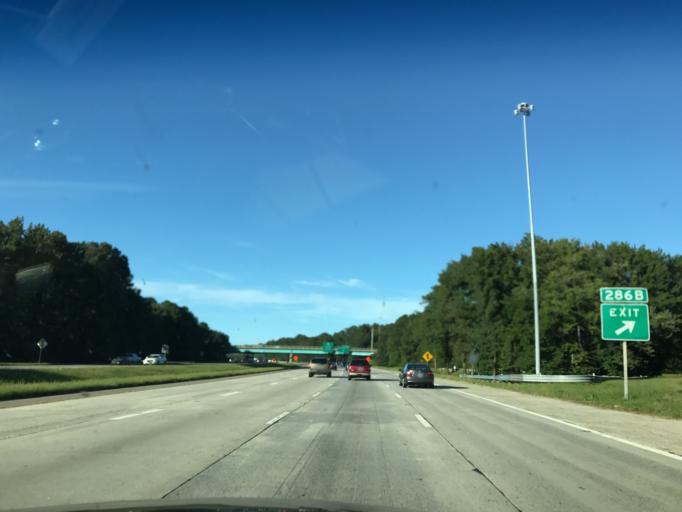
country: US
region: Virginia
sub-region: City of Chesapeake
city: Chesapeake
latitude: 36.8047
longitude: -76.1967
